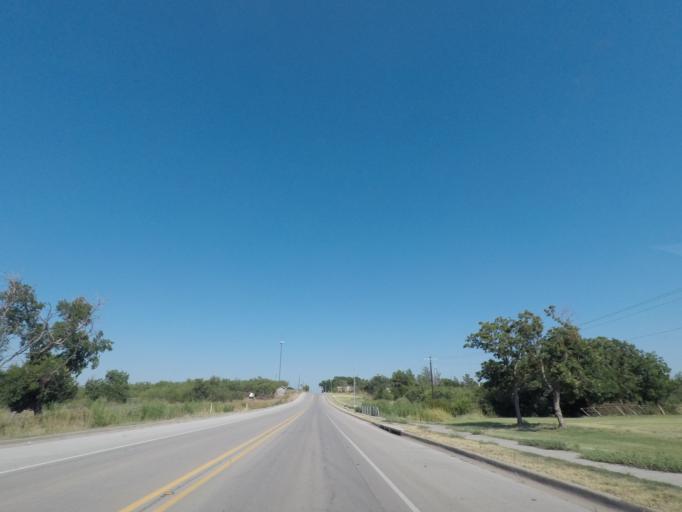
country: US
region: Texas
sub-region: Baylor County
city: Seymour
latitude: 33.5961
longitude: -99.2542
